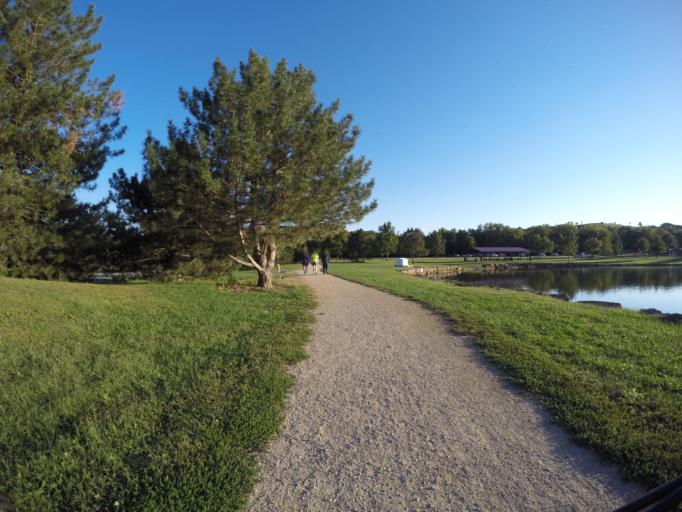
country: US
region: Kansas
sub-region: Riley County
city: Manhattan
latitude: 39.1839
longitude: -96.6295
